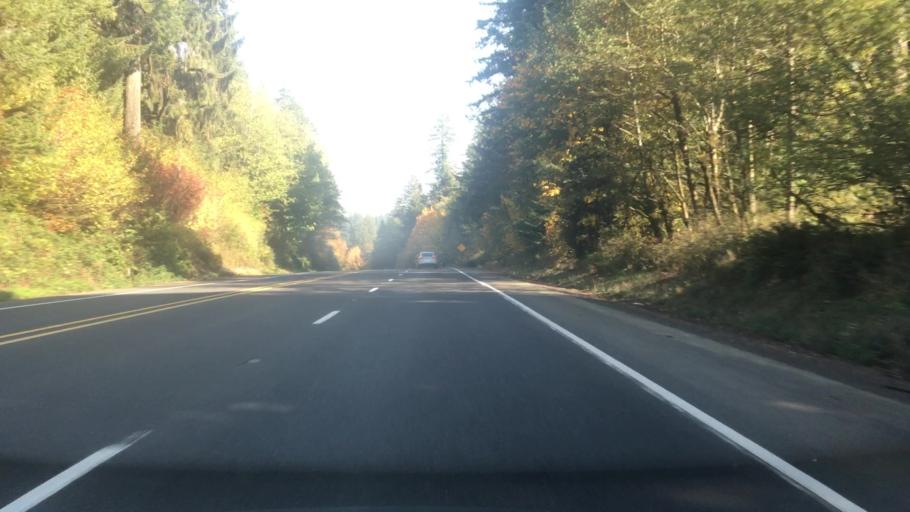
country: US
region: Oregon
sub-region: Lincoln County
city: Rose Lodge
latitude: 45.0490
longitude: -123.7878
